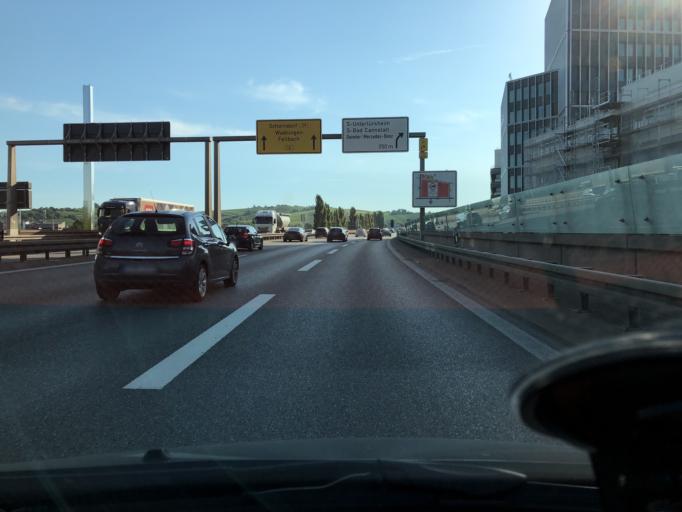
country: DE
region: Baden-Wuerttemberg
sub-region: Regierungsbezirk Stuttgart
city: Stuttgart-Ost
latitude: 48.7872
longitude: 9.2343
